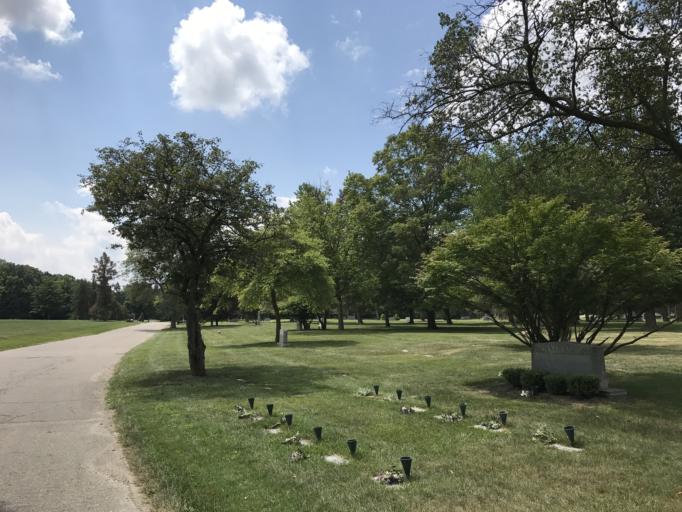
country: US
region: Michigan
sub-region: Oakland County
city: Franklin
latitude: 42.4842
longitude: -83.2999
